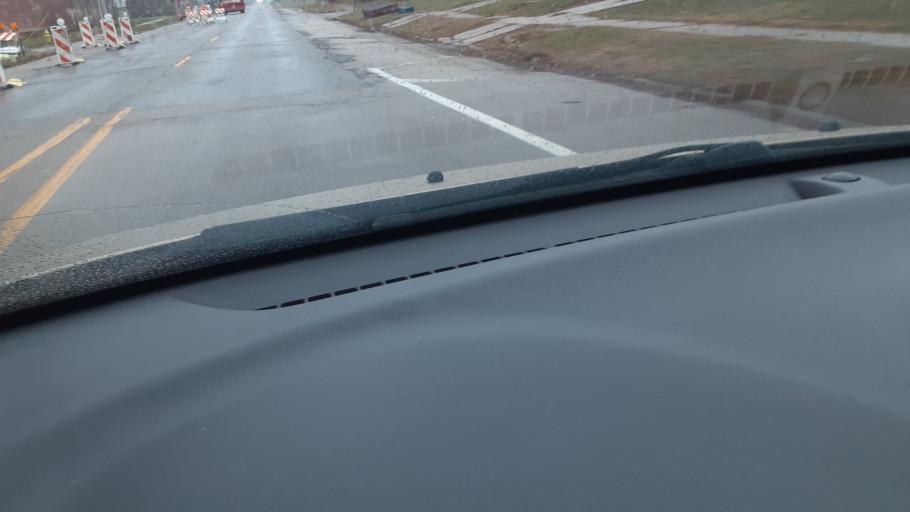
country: US
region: Illinois
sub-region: Winnebago County
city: Rockford
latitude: 42.2763
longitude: -89.1189
